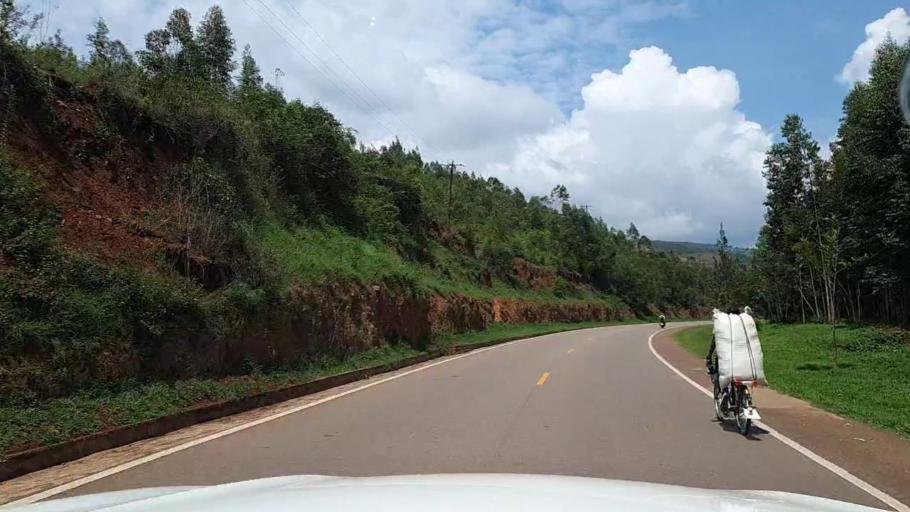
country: RW
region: Kigali
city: Kigali
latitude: -1.8422
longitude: 30.0859
